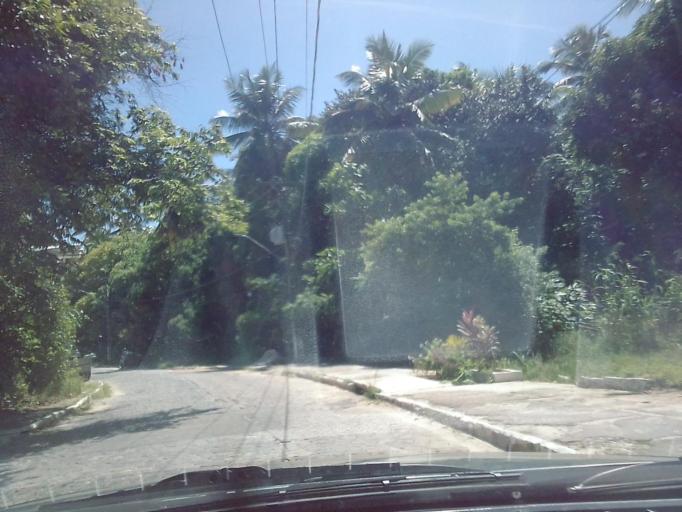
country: BR
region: Pernambuco
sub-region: Igarassu
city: Igarassu
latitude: -7.8439
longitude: -34.8445
